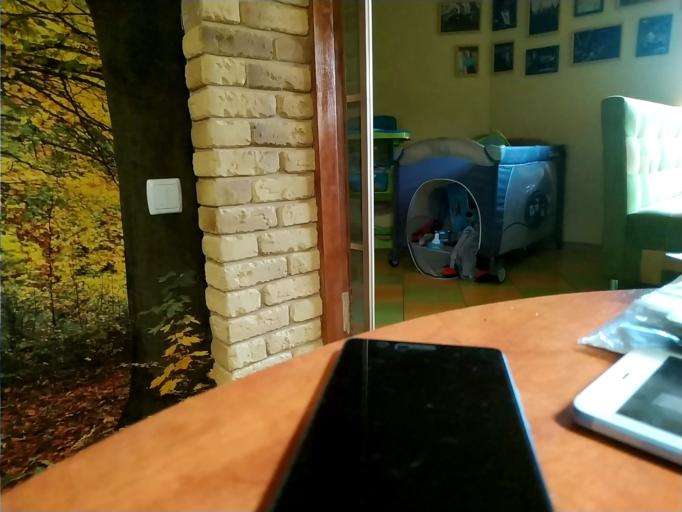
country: RU
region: Kaluga
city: Seredeyskiy
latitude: 53.7790
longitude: 35.4014
